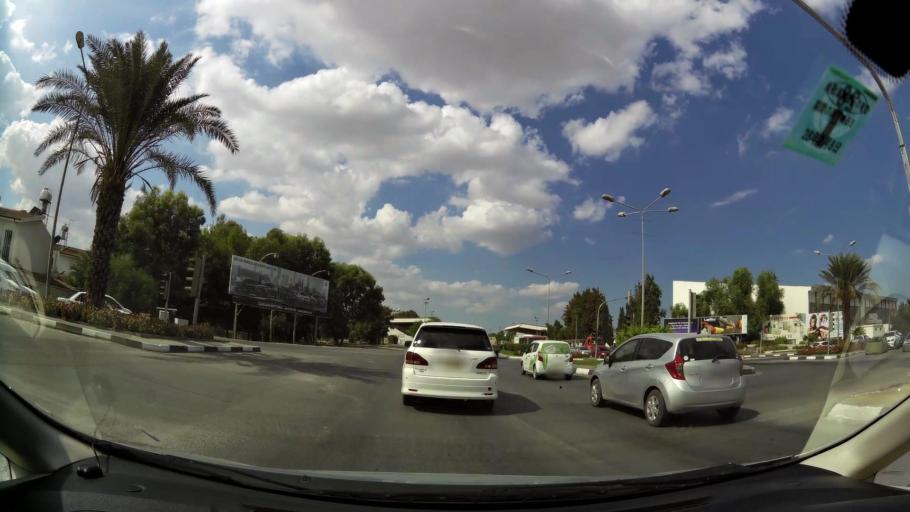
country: CY
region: Lefkosia
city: Nicosia
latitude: 35.2112
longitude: 33.3393
